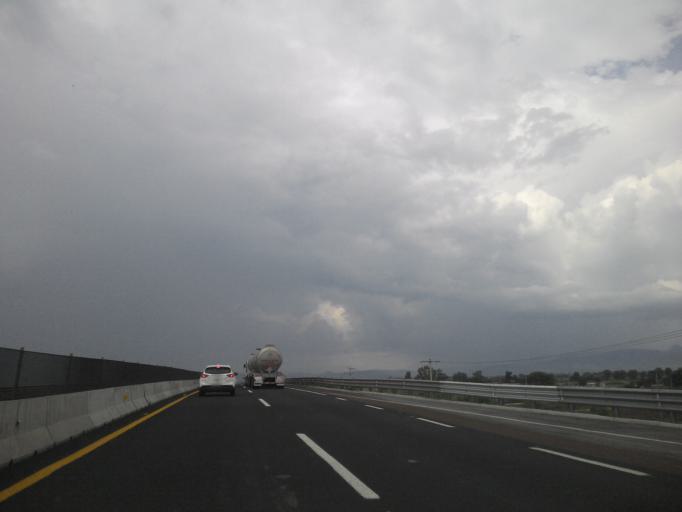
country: MX
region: Hidalgo
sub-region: Tula de Allende
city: Residencial Arboledas
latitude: 20.0959
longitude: -99.2955
